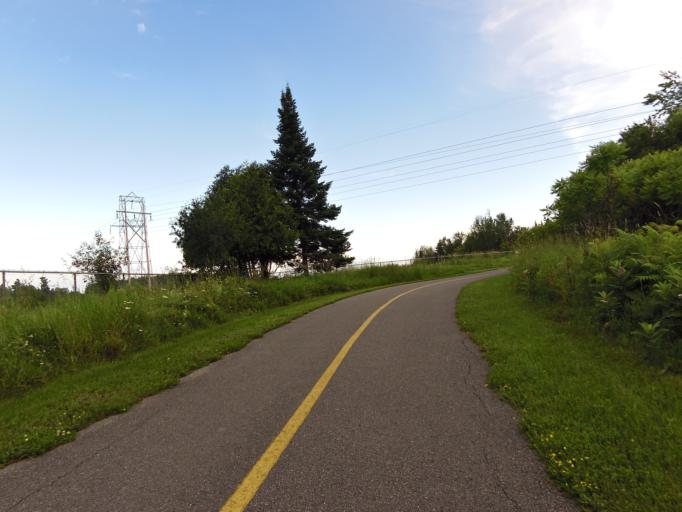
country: CA
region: Ontario
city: Bells Corners
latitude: 45.3313
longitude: -75.8880
